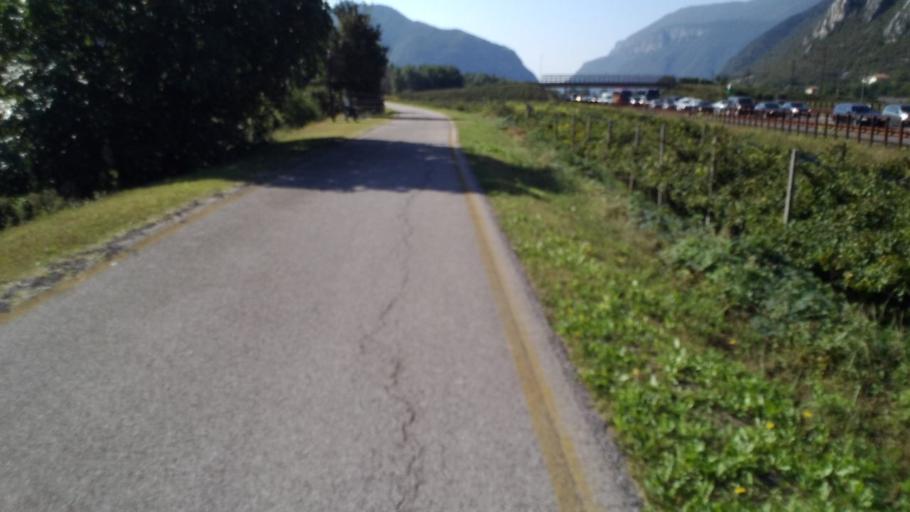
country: IT
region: Trentino-Alto Adige
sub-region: Provincia di Trento
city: Avio
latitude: 45.7191
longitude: 10.9350
